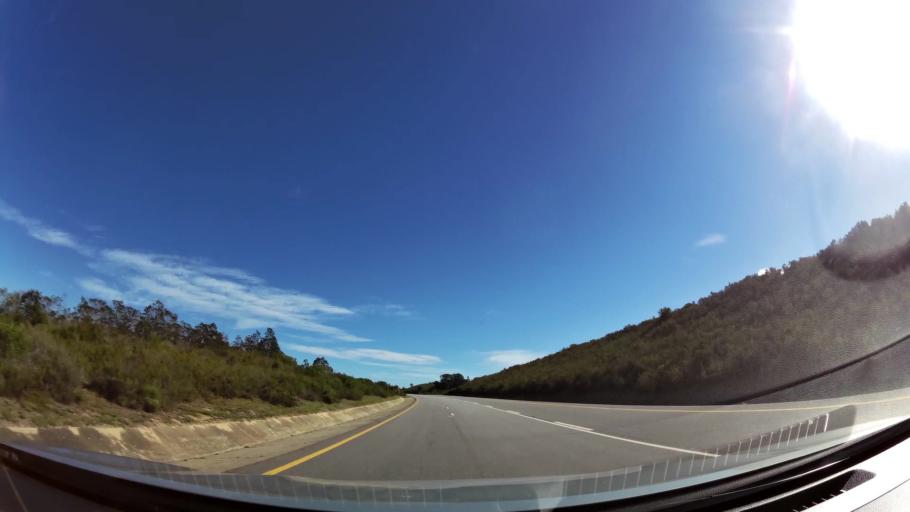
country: ZA
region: Eastern Cape
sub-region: Cacadu District Municipality
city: Kruisfontein
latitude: -34.0144
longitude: 24.6339
